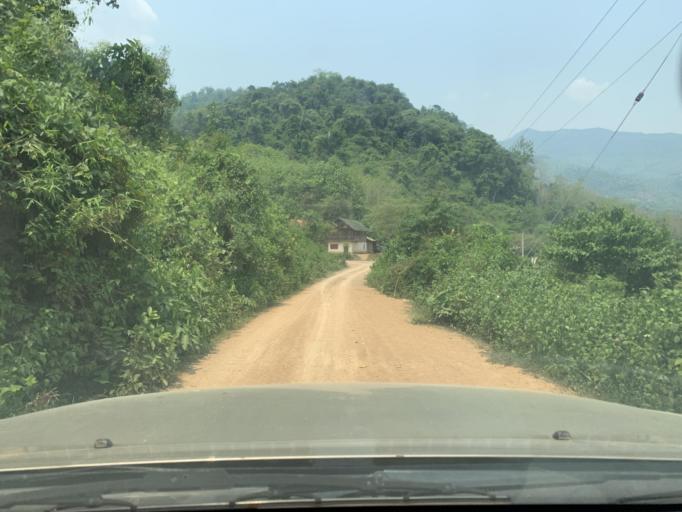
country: LA
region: Louangphabang
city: Louangphabang
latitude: 19.9696
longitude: 102.1254
